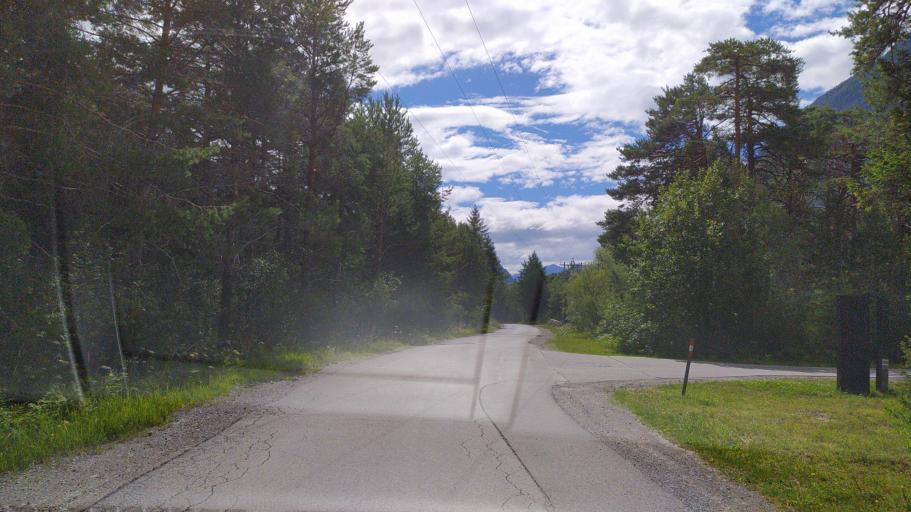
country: AT
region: Tyrol
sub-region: Politischer Bezirk Lienz
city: Lavant
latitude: 46.7907
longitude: 12.8663
